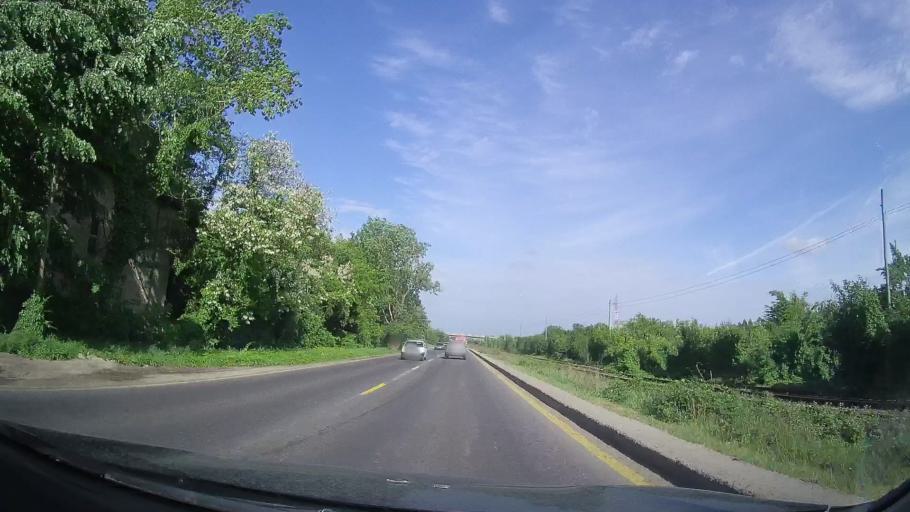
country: RO
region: Ilfov
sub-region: Comuna Magurele
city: Magurele
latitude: 44.3574
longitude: 26.0420
